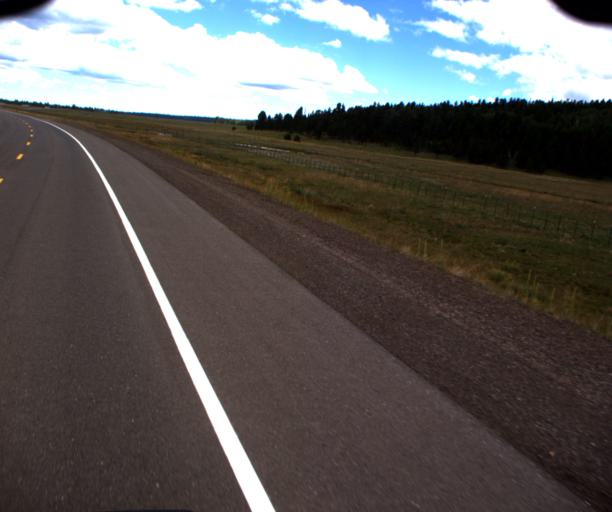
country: US
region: Arizona
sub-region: Apache County
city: Eagar
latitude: 34.0171
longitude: -109.5699
